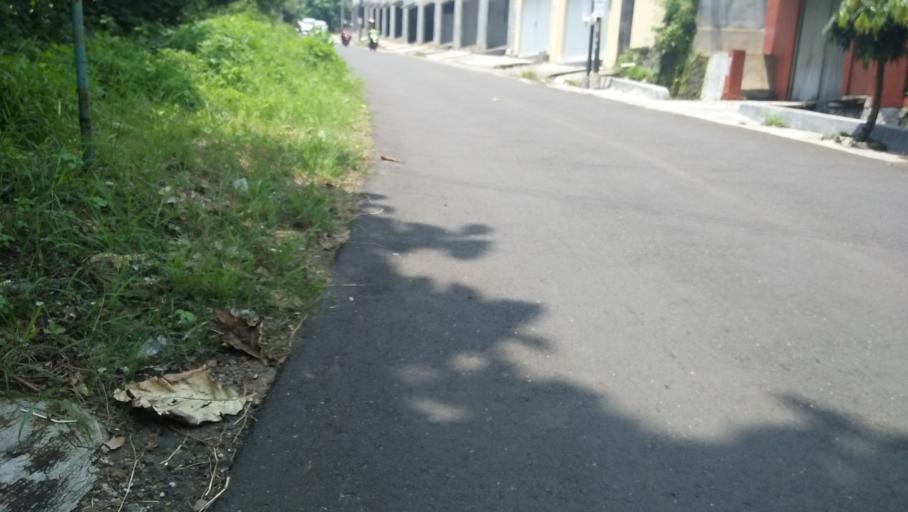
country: ID
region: Central Java
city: Semarang
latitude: -7.0354
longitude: 110.4561
